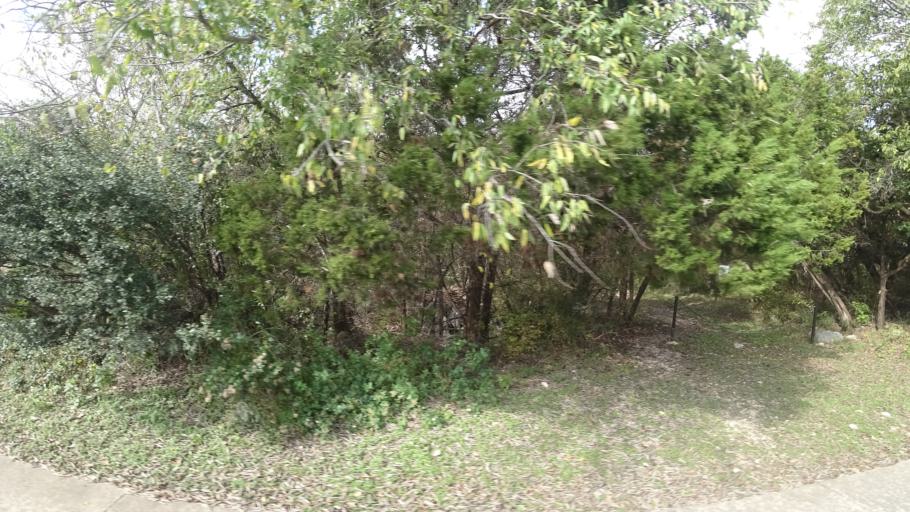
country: US
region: Texas
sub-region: Travis County
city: Barton Creek
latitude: 30.2981
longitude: -97.8938
